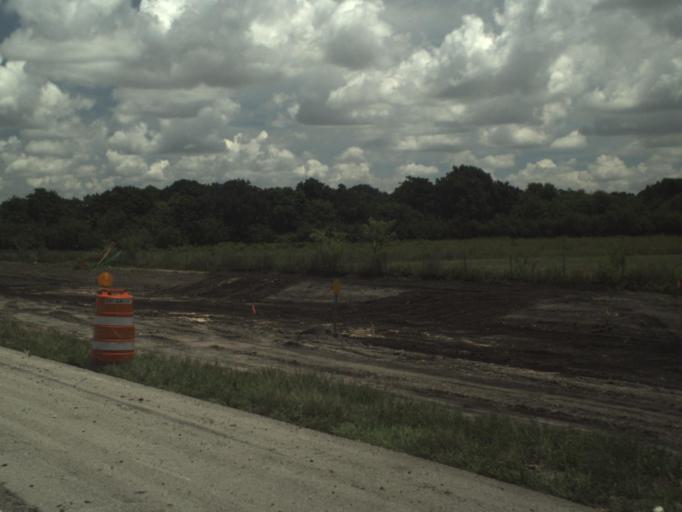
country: US
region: Florida
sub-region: Broward County
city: Southwest Ranches
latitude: 26.0730
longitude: -80.3585
